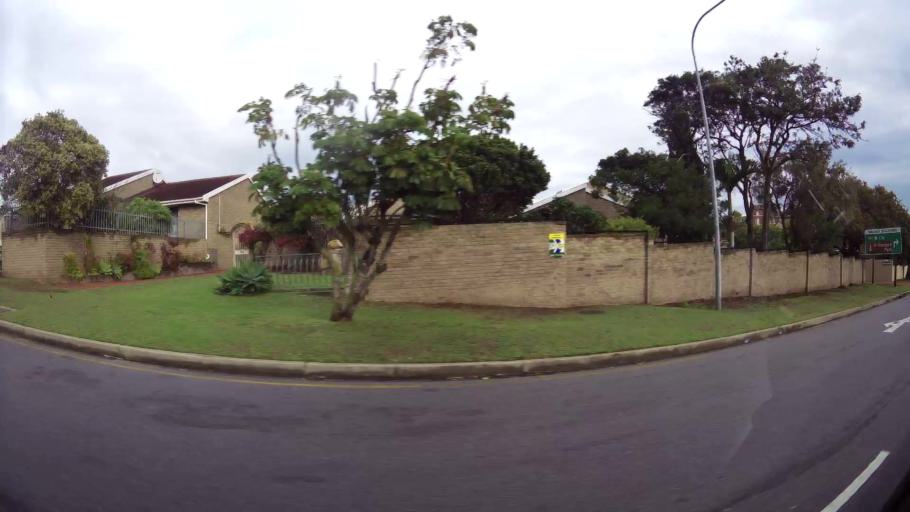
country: ZA
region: Eastern Cape
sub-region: Nelson Mandela Bay Metropolitan Municipality
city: Port Elizabeth
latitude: -33.9713
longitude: 25.6270
